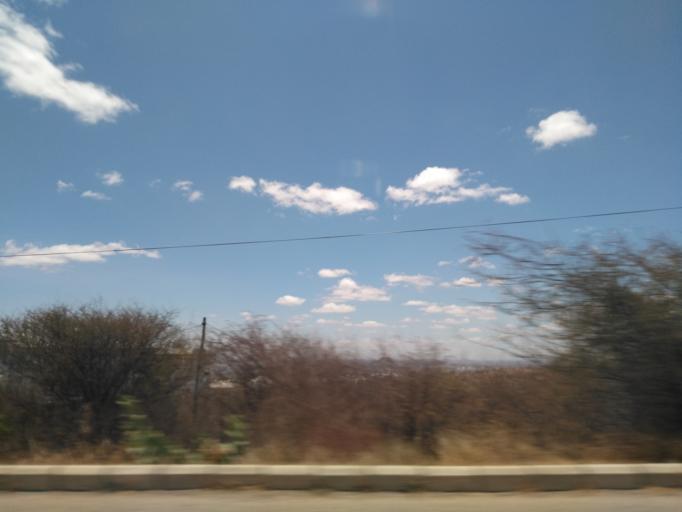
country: TZ
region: Dodoma
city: Kisasa
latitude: -6.2155
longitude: 35.7914
